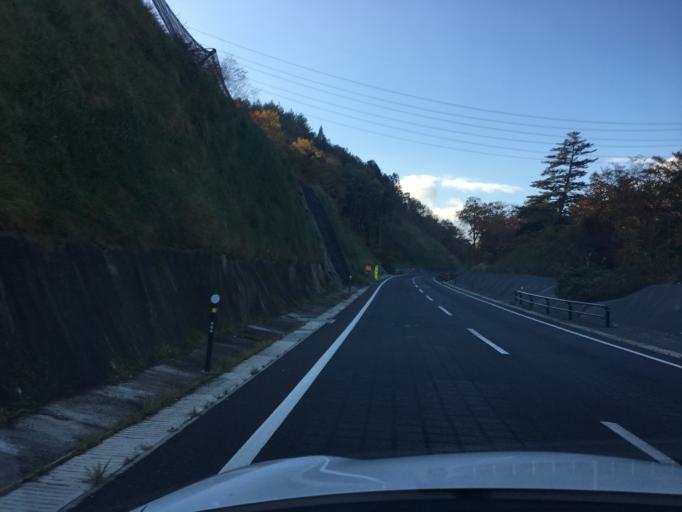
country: JP
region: Fukushima
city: Funehikimachi-funehiki
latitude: 37.2893
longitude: 140.7549
